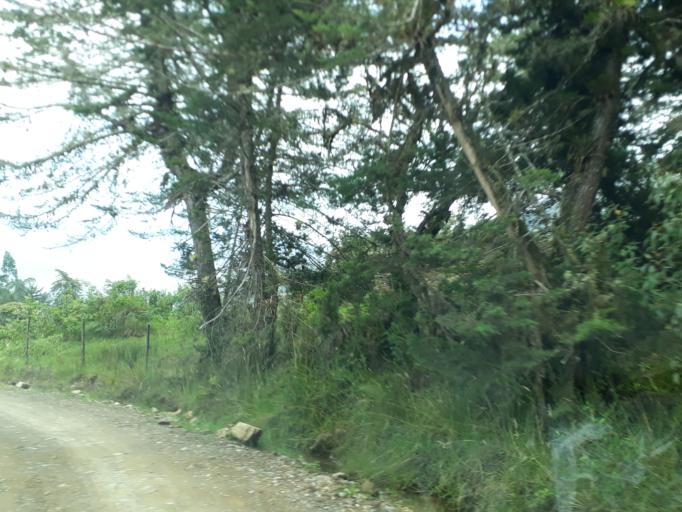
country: CO
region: Cundinamarca
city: Macheta
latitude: 5.1037
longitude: -73.5410
